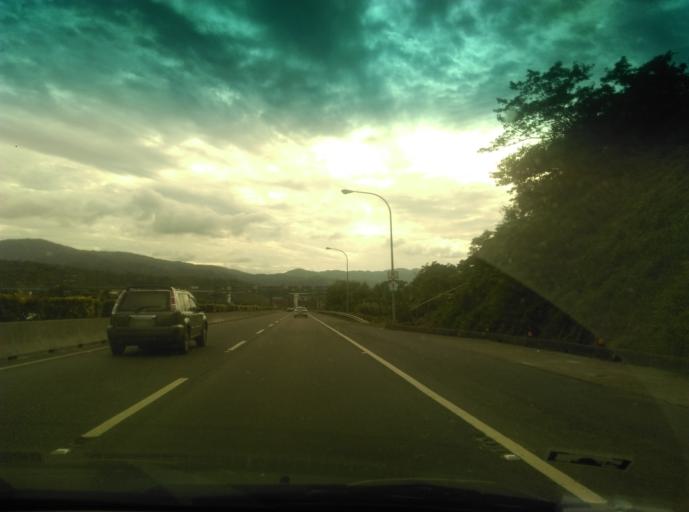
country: TW
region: Taiwan
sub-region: Keelung
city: Keelung
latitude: 25.1109
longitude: 121.7265
